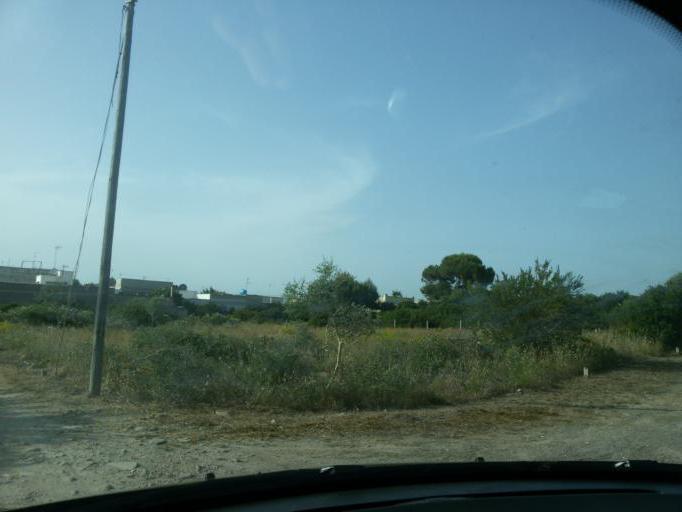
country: IT
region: Apulia
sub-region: Provincia di Lecce
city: Porto Cesareo
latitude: 40.2334
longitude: 17.9145
